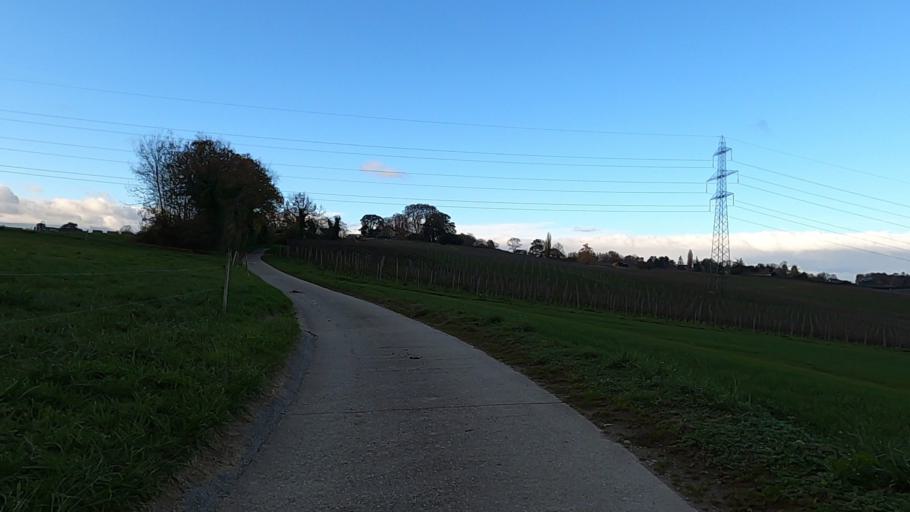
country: CH
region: Vaud
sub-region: Morges District
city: Saint-Prex
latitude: 46.5135
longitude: 6.4632
